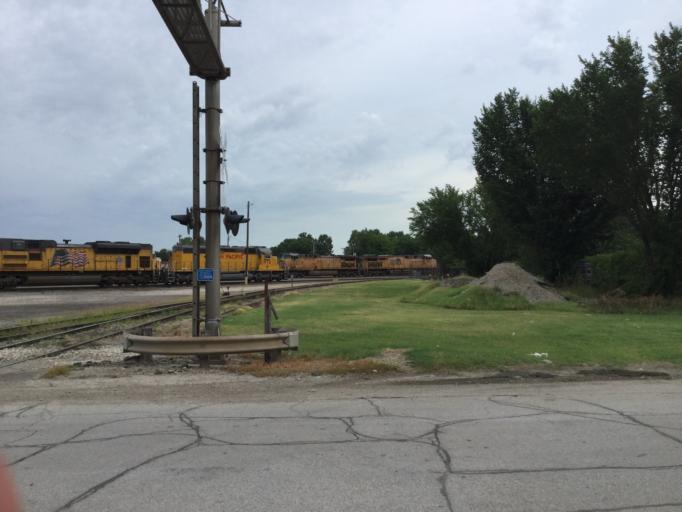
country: US
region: Kansas
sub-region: Montgomery County
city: Coffeyville
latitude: 37.0289
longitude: -95.6233
